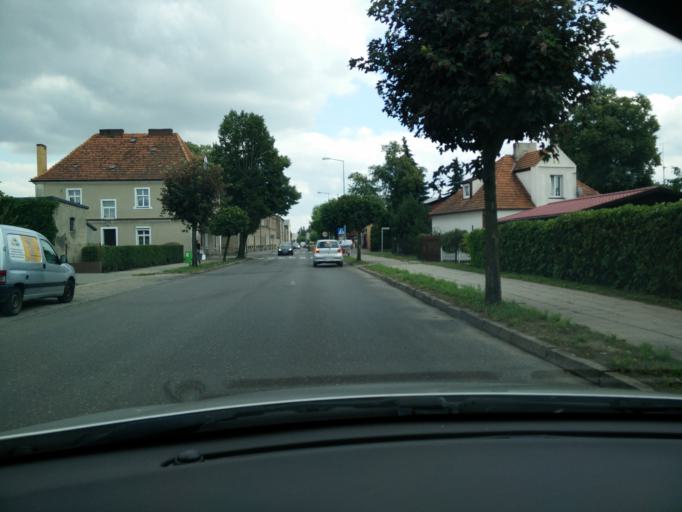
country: PL
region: Greater Poland Voivodeship
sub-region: Powiat sredzki
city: Sroda Wielkopolska
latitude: 52.2281
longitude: 17.2681
